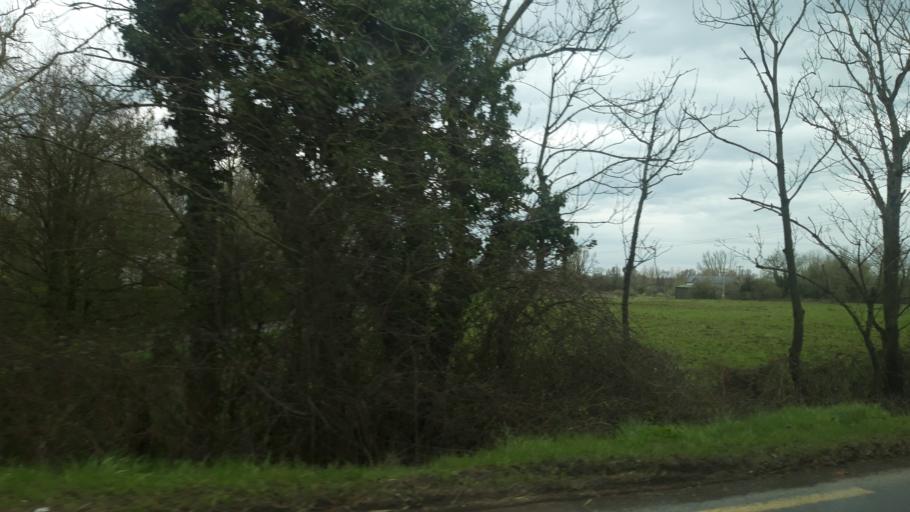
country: IE
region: Leinster
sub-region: Kildare
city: Prosperous
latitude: 53.2929
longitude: -6.7499
